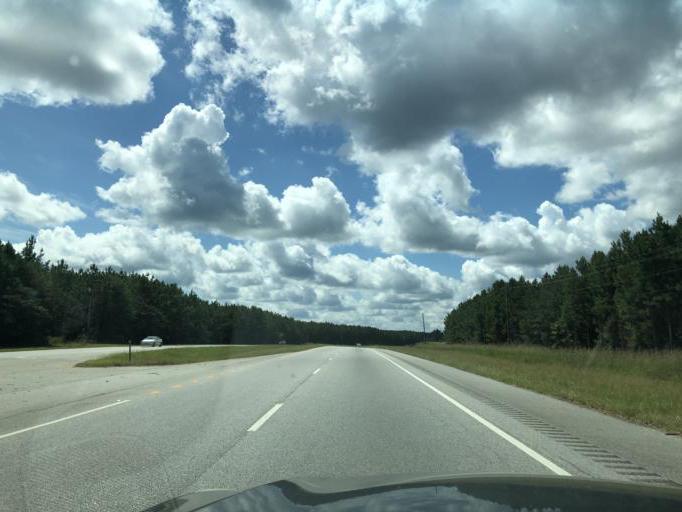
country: US
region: Alabama
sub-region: Russell County
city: Ladonia
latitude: 32.2199
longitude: -85.1694
